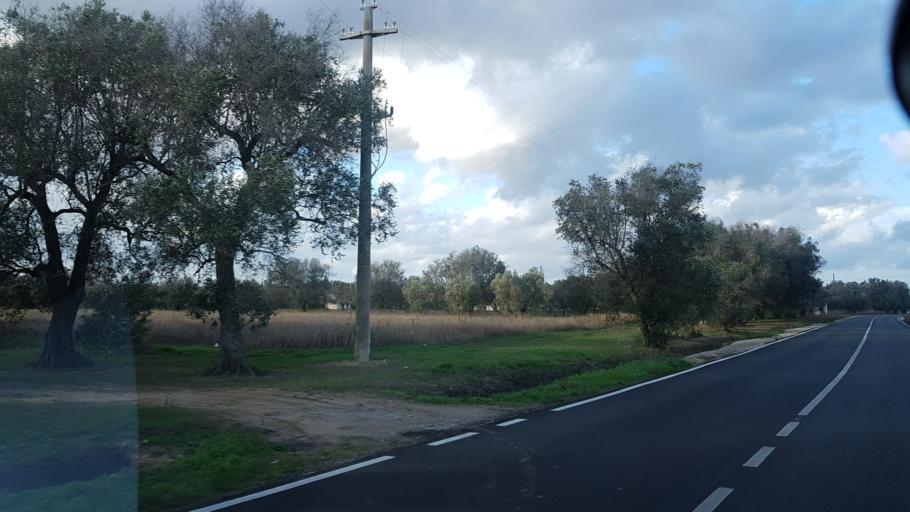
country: IT
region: Apulia
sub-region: Provincia di Brindisi
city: San Pietro Vernotico
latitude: 40.5055
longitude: 18.0079
